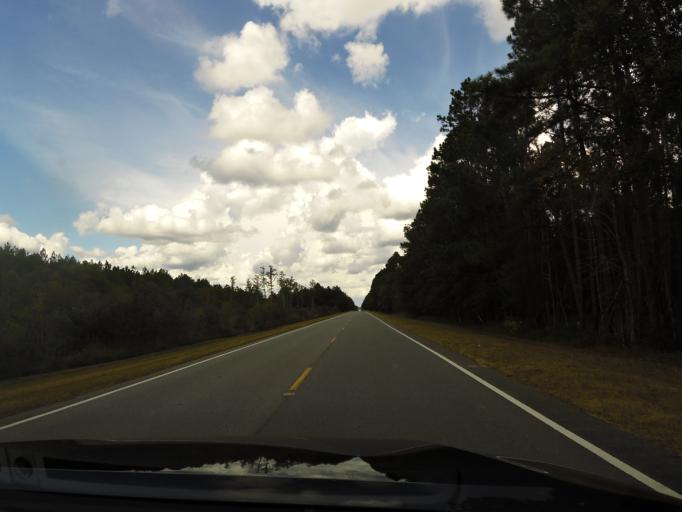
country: US
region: Georgia
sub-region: Charlton County
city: Folkston
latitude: 30.9509
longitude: -82.0232
